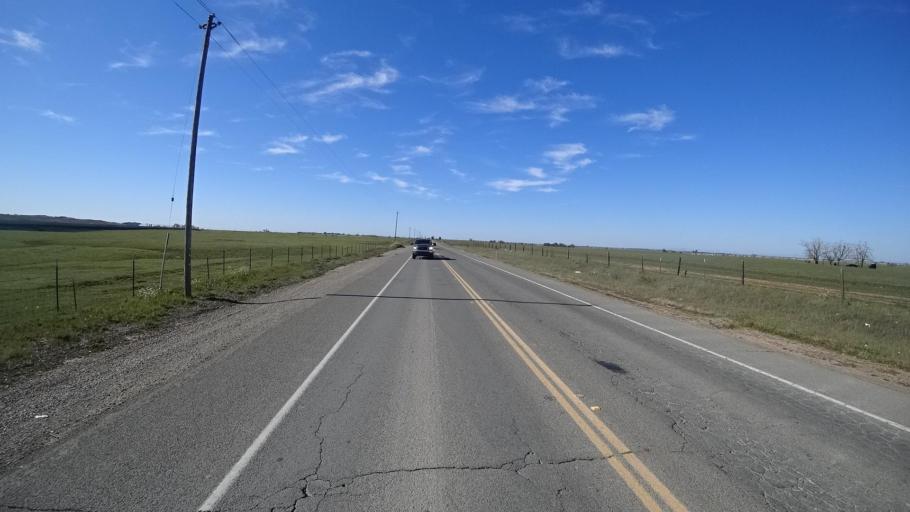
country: US
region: California
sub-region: Sacramento County
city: Rancho Murieta
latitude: 38.5302
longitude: -121.1919
